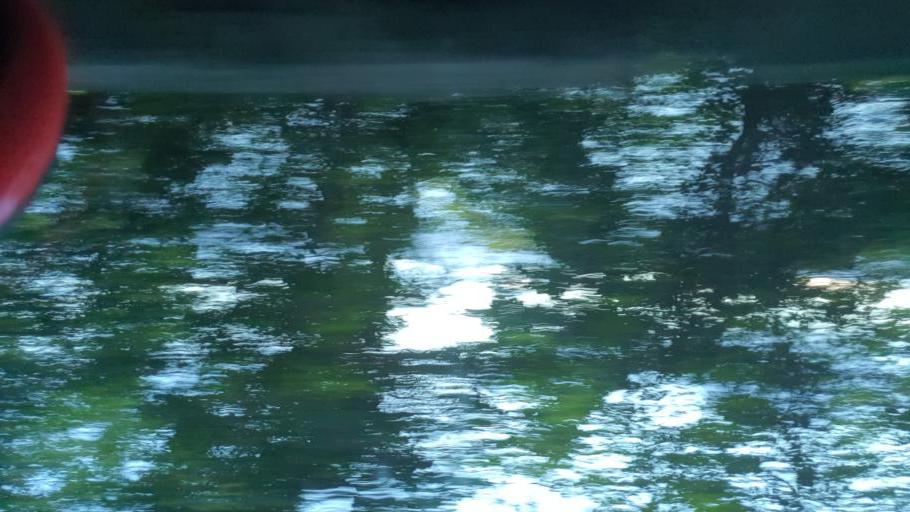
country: GB
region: Northern Ireland
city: Rostrevor
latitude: 54.0913
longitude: -6.1897
